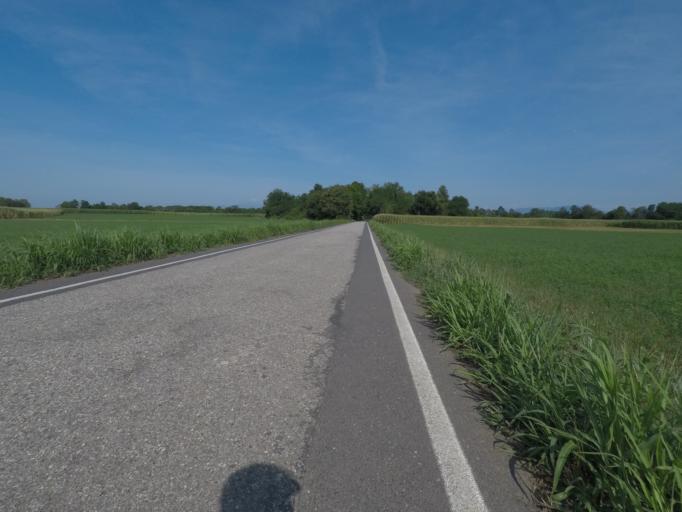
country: IT
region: Friuli Venezia Giulia
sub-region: Provincia di Udine
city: Basiliano-Vissandone
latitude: 46.0637
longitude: 13.0999
